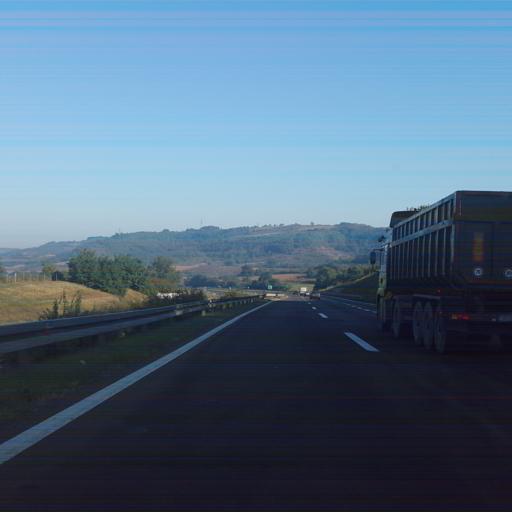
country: RS
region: Central Serbia
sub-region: Belgrade
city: Grocka
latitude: 44.6472
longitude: 20.6287
